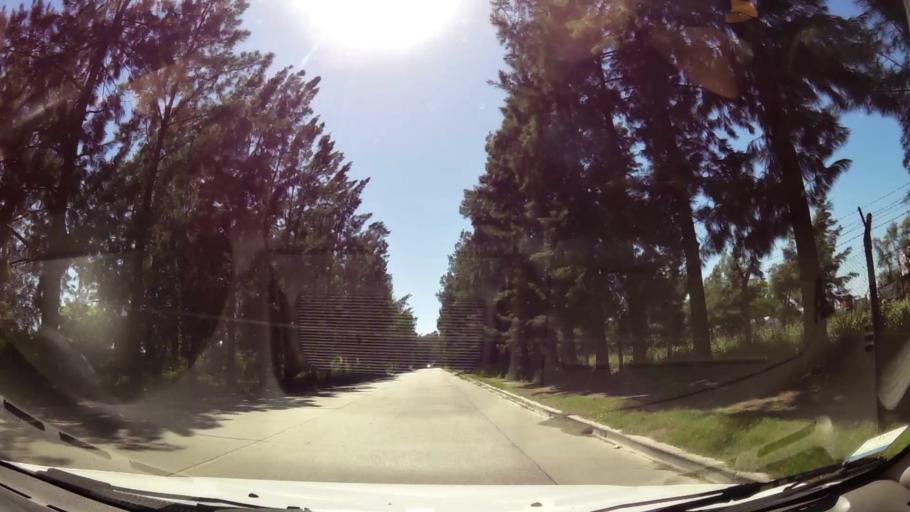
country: AR
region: Buenos Aires F.D.
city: Buenos Aires
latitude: -34.6241
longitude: -58.3495
